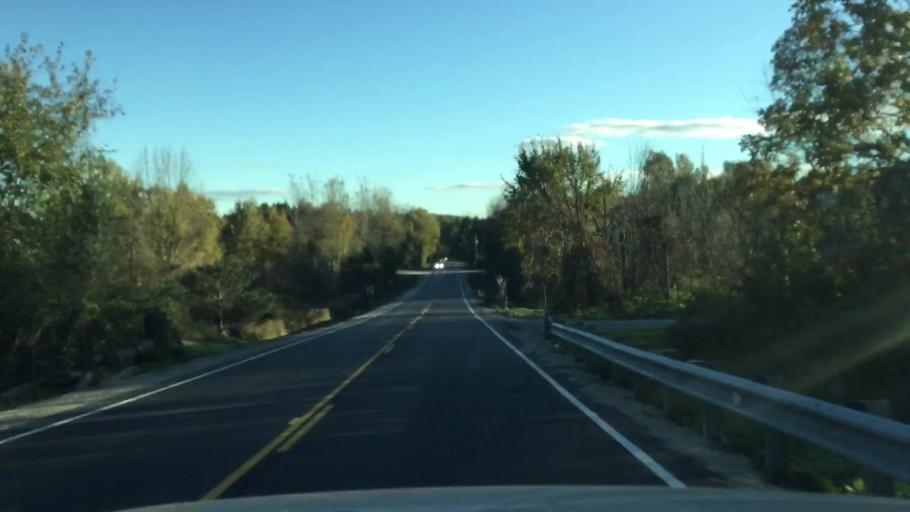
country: US
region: Michigan
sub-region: Lapeer County
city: Almont
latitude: 42.9044
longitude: -83.1428
